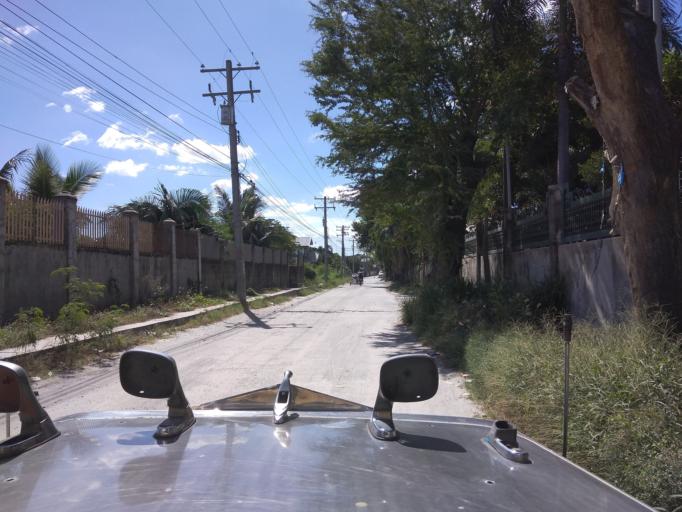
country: PH
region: Central Luzon
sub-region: Province of Pampanga
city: Magliman
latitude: 15.0388
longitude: 120.6570
